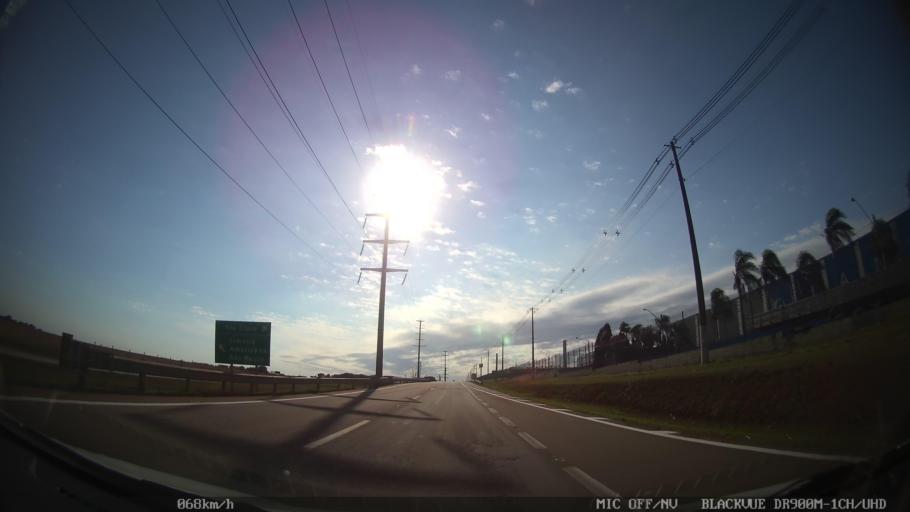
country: BR
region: Sao Paulo
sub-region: Piracicaba
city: Piracicaba
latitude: -22.6631
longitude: -47.6086
